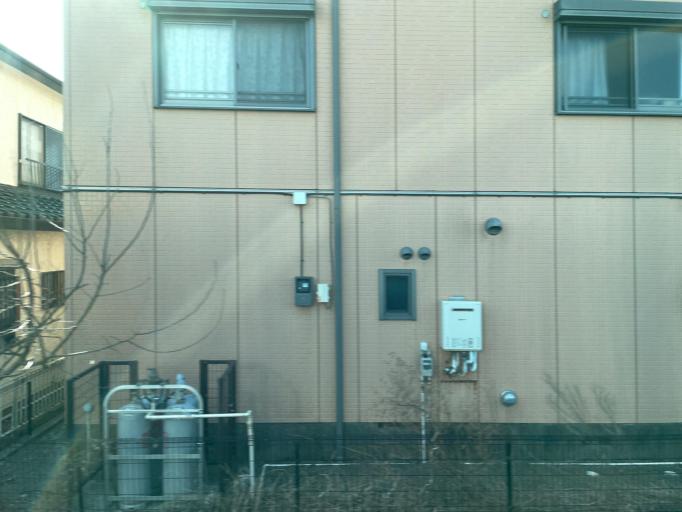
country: JP
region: Kanagawa
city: Chigasaki
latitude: 35.3642
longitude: 139.3924
